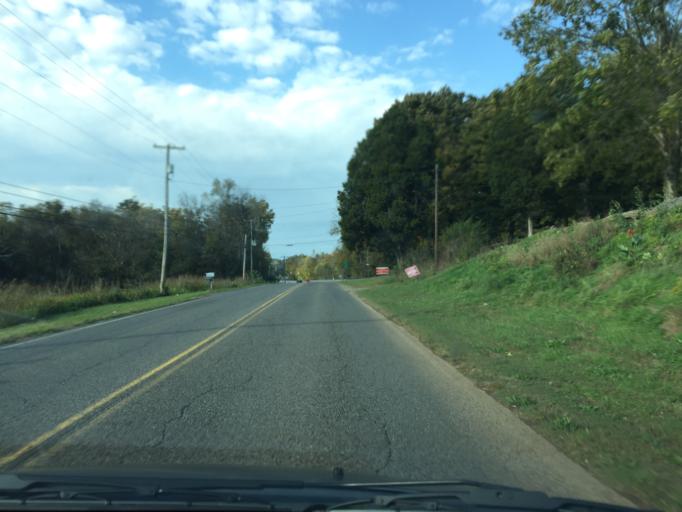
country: US
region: Tennessee
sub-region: Loudon County
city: Loudon
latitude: 35.7183
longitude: -84.3471
